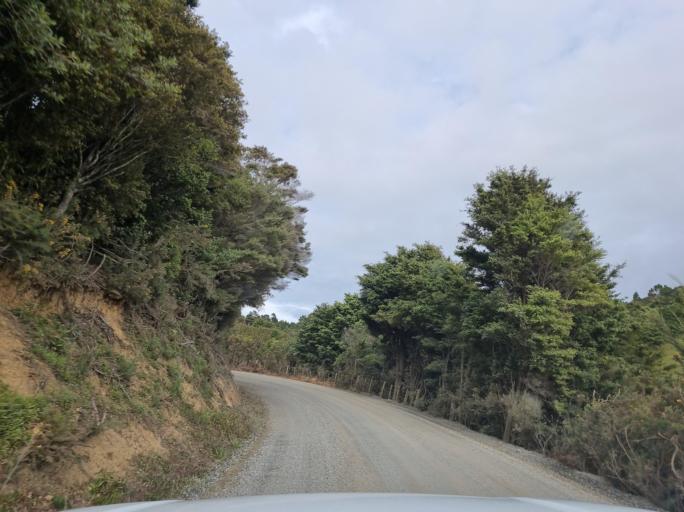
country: NZ
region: Northland
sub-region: Whangarei
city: Ruakaka
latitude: -36.0398
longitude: 174.4098
